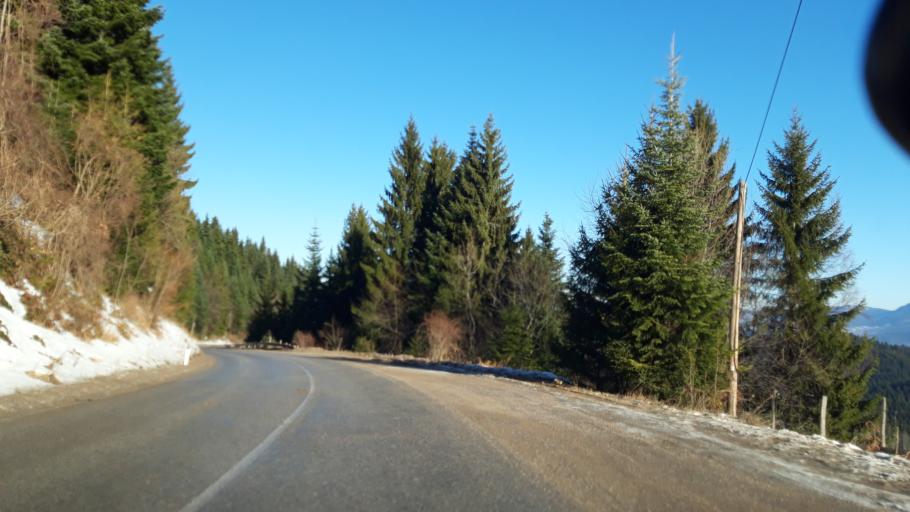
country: BA
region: Republika Srpska
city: Koran
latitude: 43.7940
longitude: 18.5557
